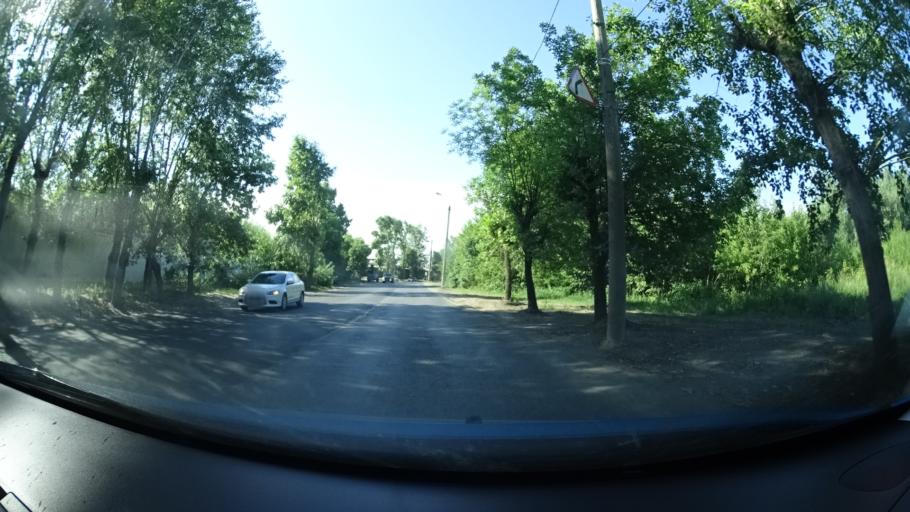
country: RU
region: Bashkortostan
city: Ufa
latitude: 54.8371
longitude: 56.0761
